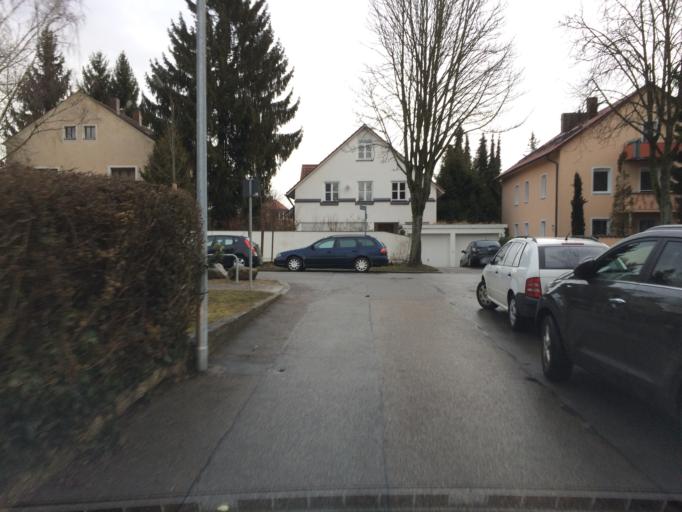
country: DE
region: Bavaria
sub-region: Upper Palatinate
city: Pentling
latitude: 49.0022
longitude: 12.0851
